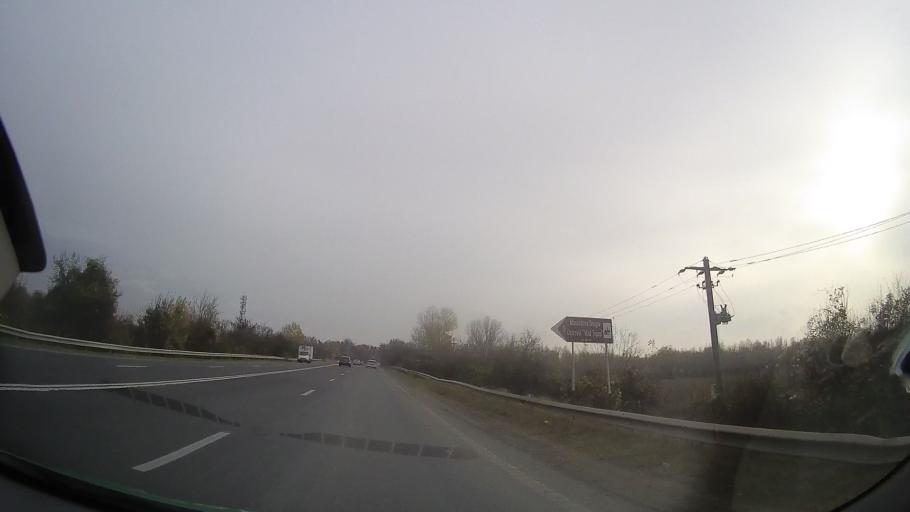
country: RO
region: Ilfov
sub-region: Comuna Ciolpani
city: Ciolpani
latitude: 44.7426
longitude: 26.1112
